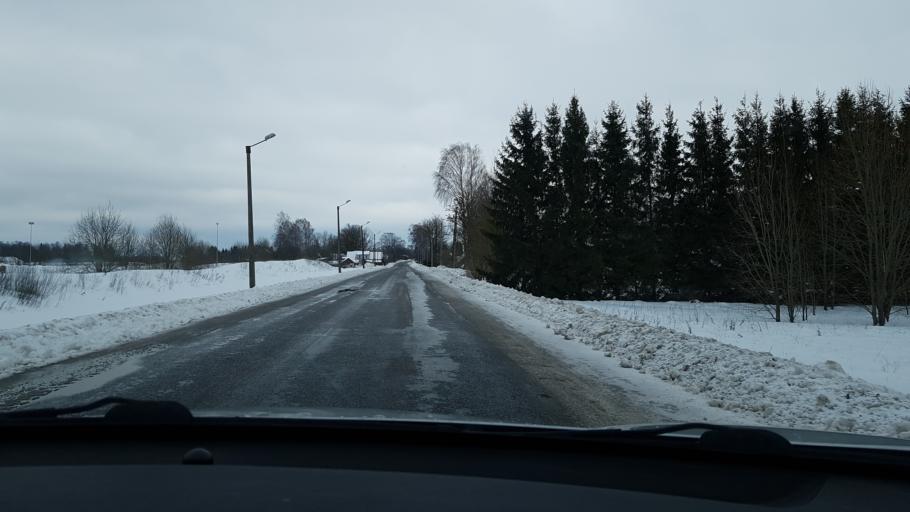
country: EE
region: Jaervamaa
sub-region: Koeru vald
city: Koeru
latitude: 58.9700
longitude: 26.0162
